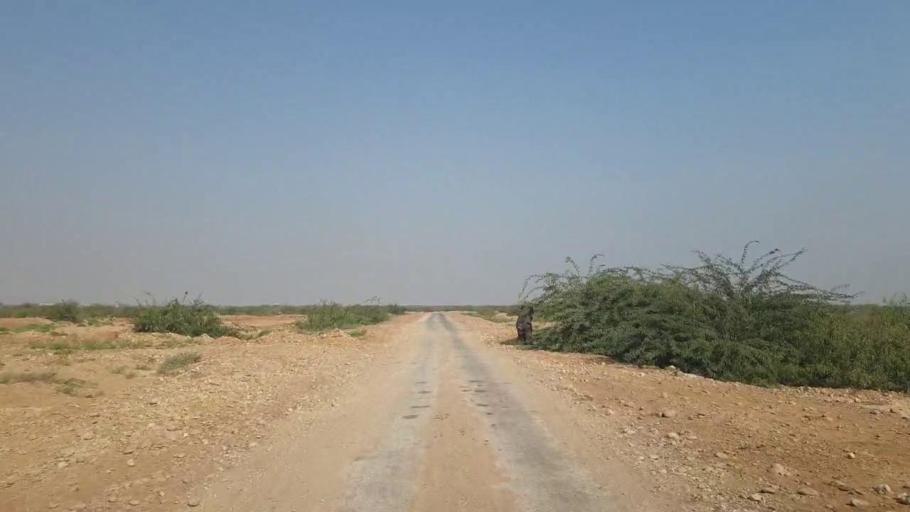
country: PK
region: Sindh
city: Jamshoro
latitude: 25.5375
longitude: 68.3446
